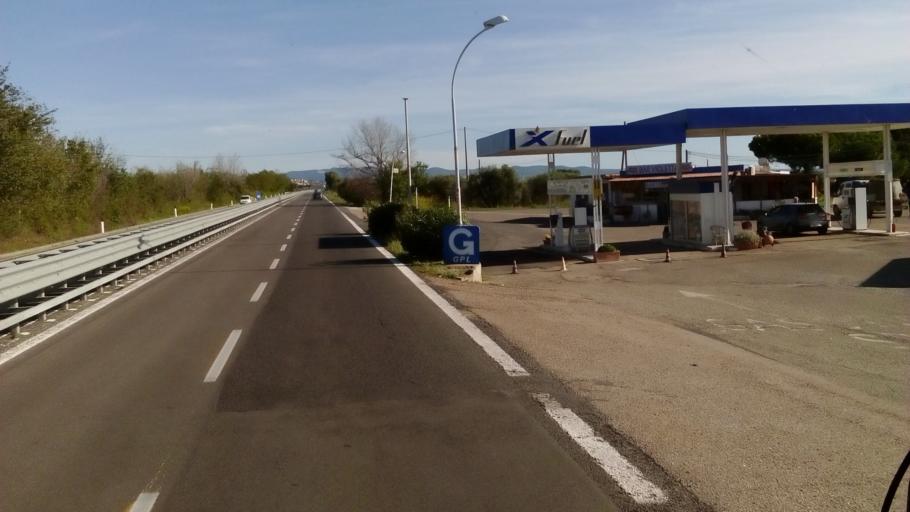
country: IT
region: Latium
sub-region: Provincia di Viterbo
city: Tarquinia
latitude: 42.2736
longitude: 11.7090
